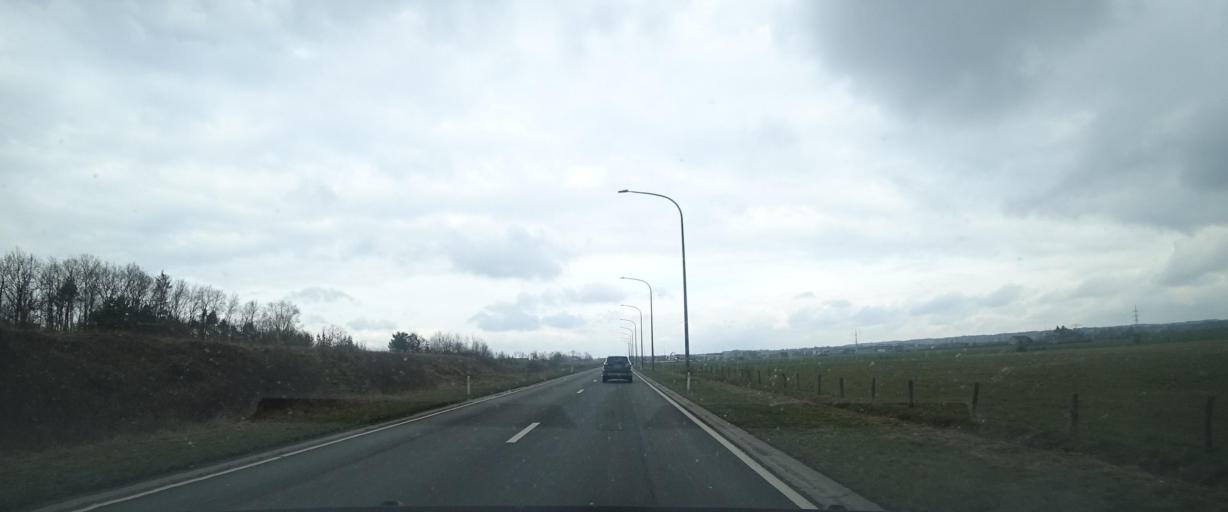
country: BE
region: Wallonia
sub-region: Province du Luxembourg
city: Marche-en-Famenne
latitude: 50.2401
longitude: 5.3285
